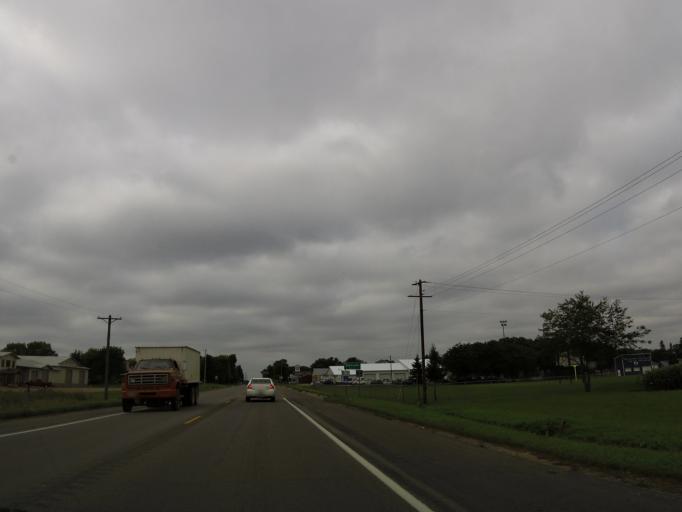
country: US
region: Minnesota
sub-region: Renville County
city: Olivia
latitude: 44.7888
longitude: -95.0924
